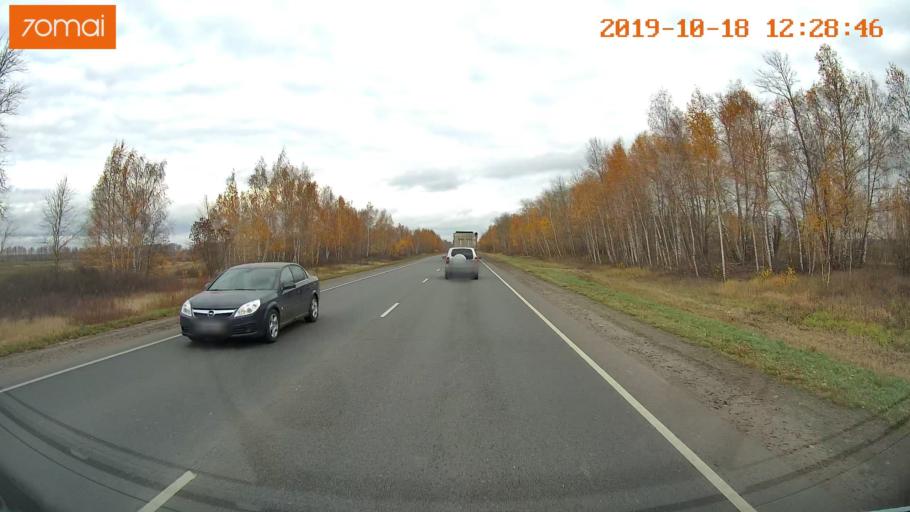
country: RU
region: Rjazan
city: Ryazan'
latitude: 54.5742
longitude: 39.5738
